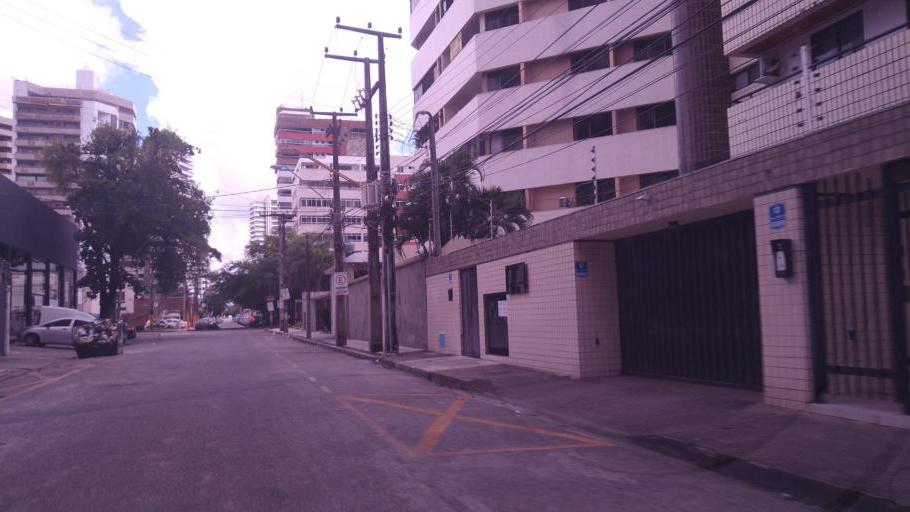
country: BR
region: Ceara
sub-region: Fortaleza
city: Fortaleza
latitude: -3.7331
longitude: -38.4911
